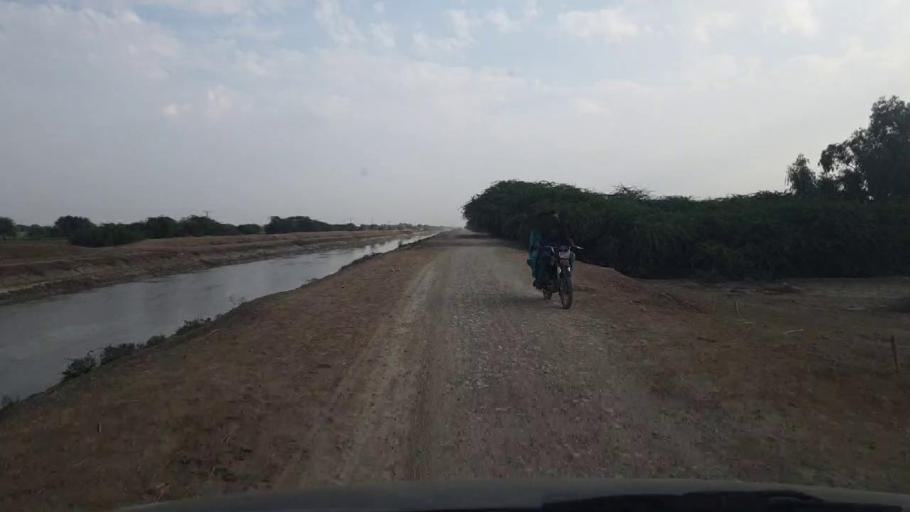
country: PK
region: Sindh
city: Badin
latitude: 24.5248
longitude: 68.6807
